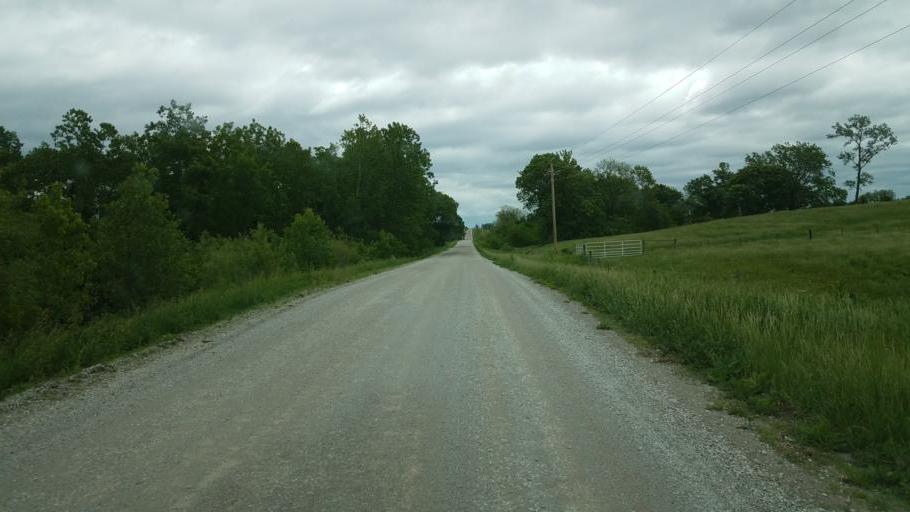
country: US
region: Iowa
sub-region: Decatur County
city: Lamoni
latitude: 40.6383
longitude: -93.8553
